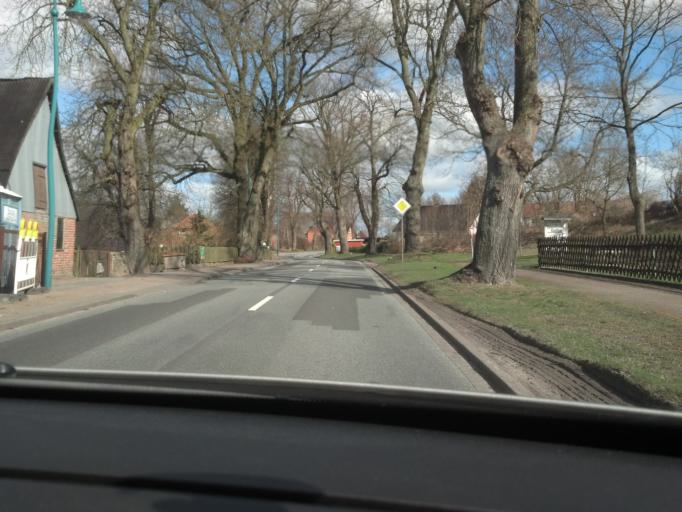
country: DE
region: Schleswig-Holstein
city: Gudow
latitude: 53.4908
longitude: 10.8320
